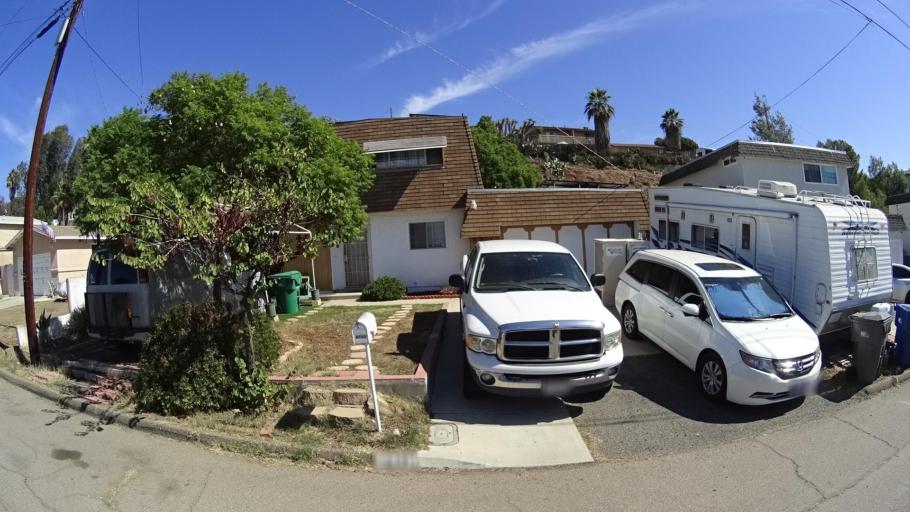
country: US
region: California
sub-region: San Diego County
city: La Presa
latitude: 32.7198
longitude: -117.0111
